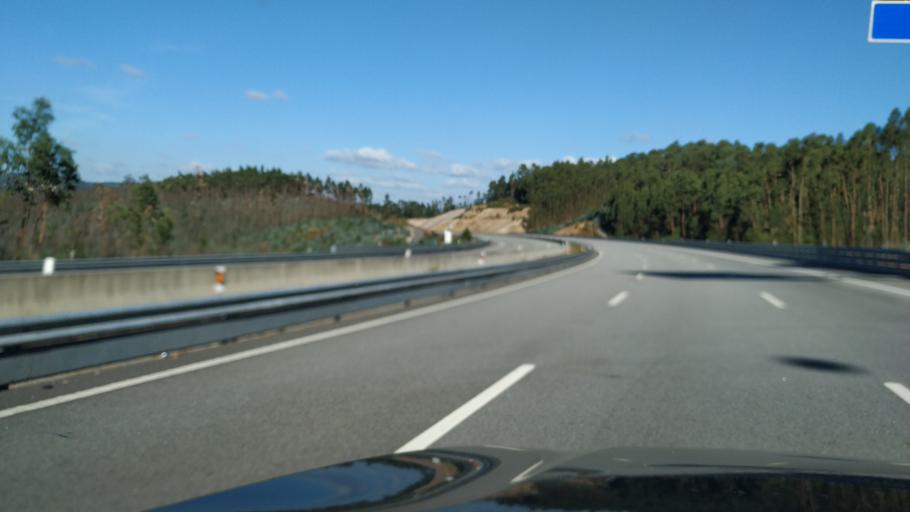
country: PT
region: Porto
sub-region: Vila Nova de Gaia
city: Sandim
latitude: 41.0230
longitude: -8.4782
